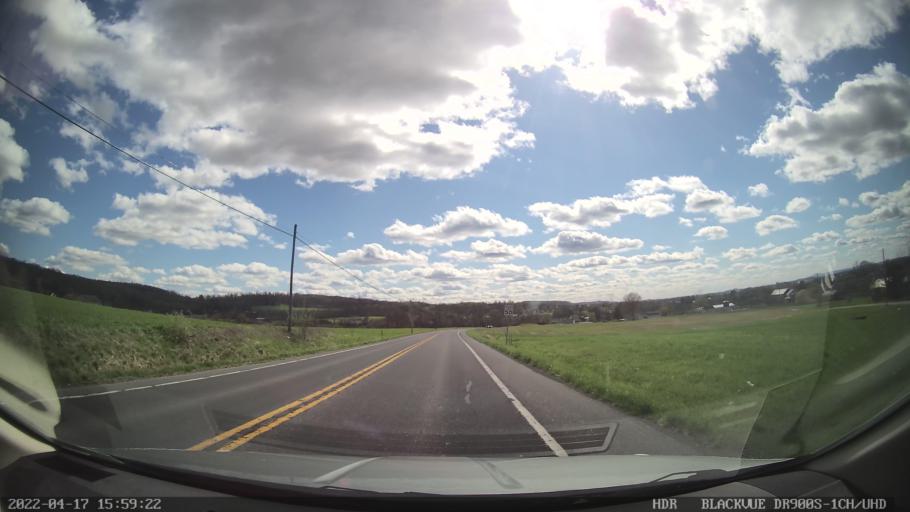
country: US
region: Pennsylvania
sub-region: Berks County
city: Topton
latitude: 40.4933
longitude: -75.7159
